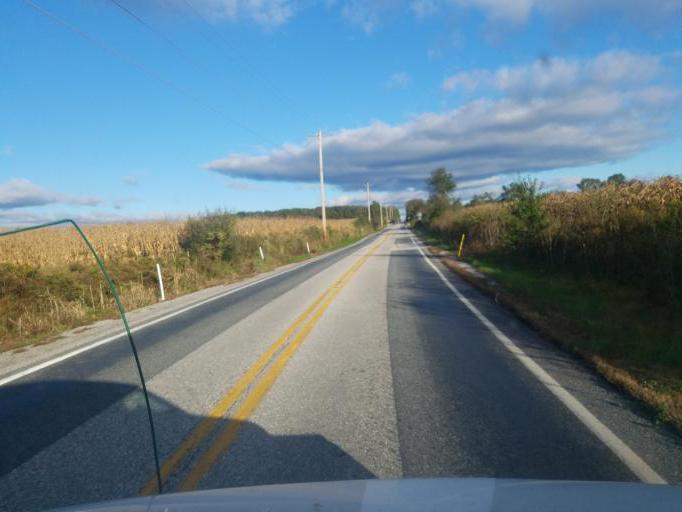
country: US
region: Pennsylvania
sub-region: Adams County
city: Biglerville
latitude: 39.8987
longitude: -77.2102
